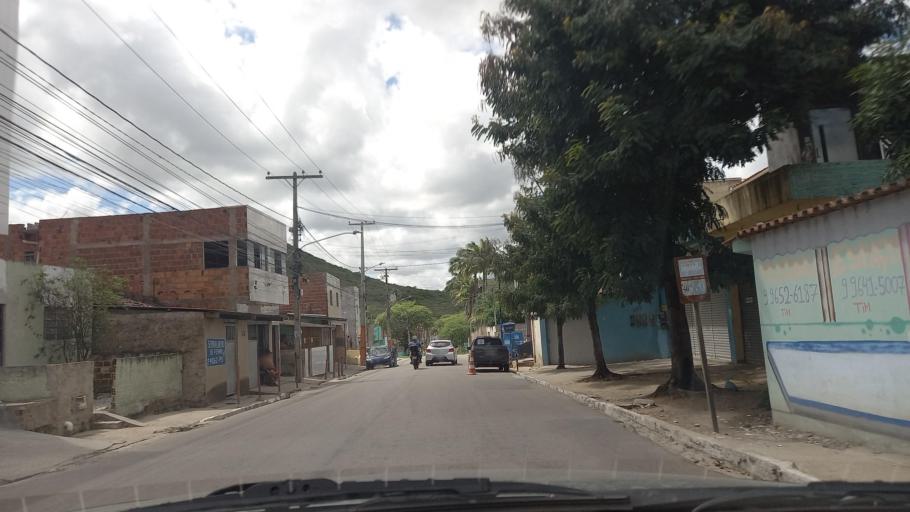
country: BR
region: Pernambuco
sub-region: Caruaru
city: Caruaru
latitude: -8.2783
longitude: -35.9441
